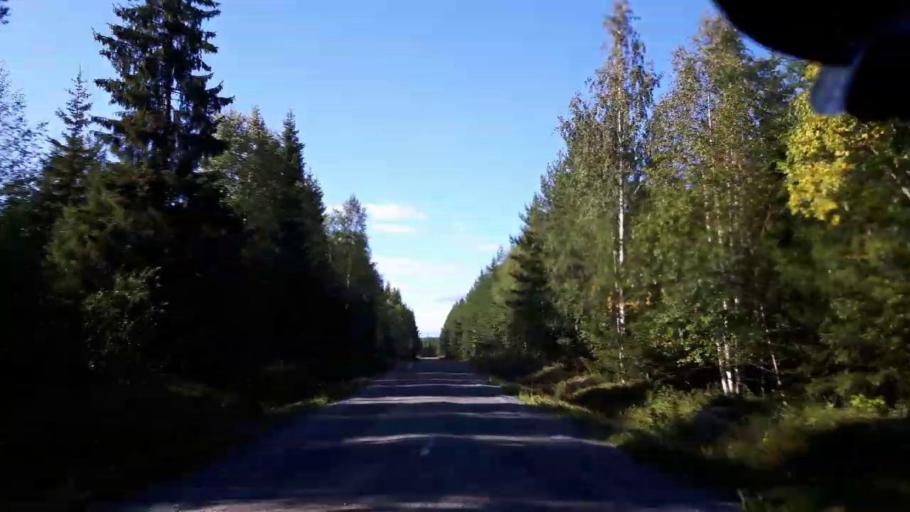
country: SE
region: Jaemtland
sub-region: Ragunda Kommun
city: Hammarstrand
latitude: 63.5314
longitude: 16.0766
